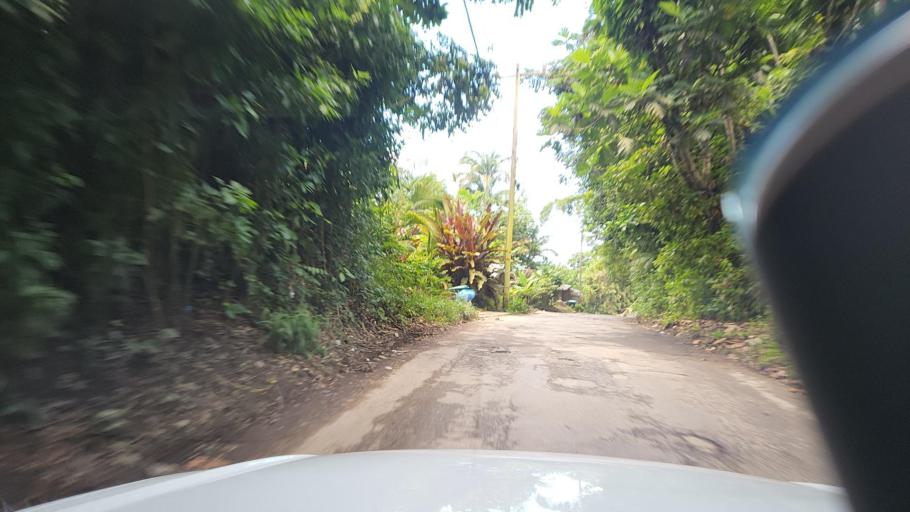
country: BB
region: Saint Thomas
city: Welchman Hall
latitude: 13.2033
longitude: -59.5594
